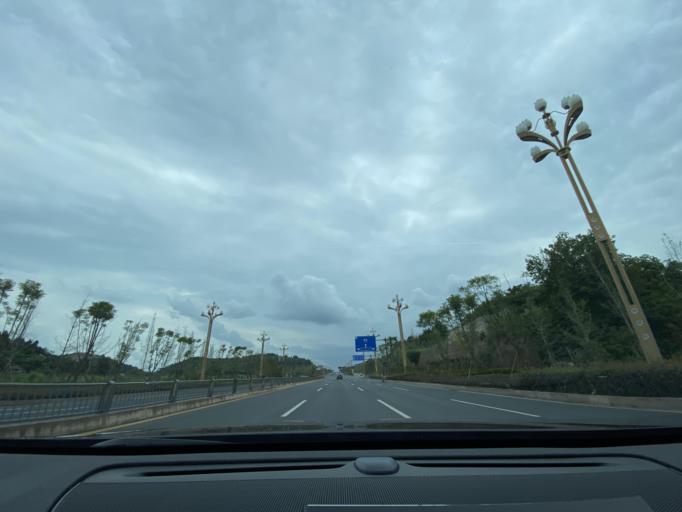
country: CN
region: Sichuan
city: Jiancheng
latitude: 30.4575
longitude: 104.4958
